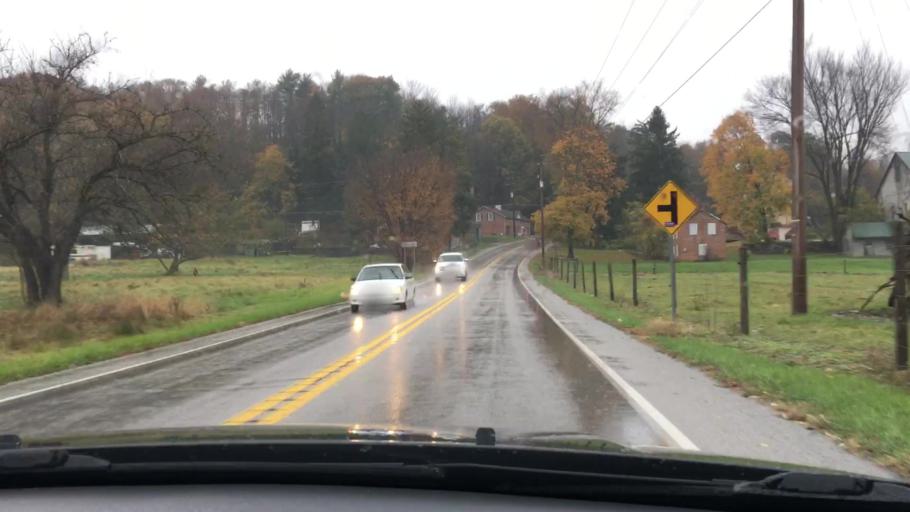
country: US
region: Pennsylvania
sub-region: York County
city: Glen Rock
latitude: 39.7467
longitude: -76.8032
